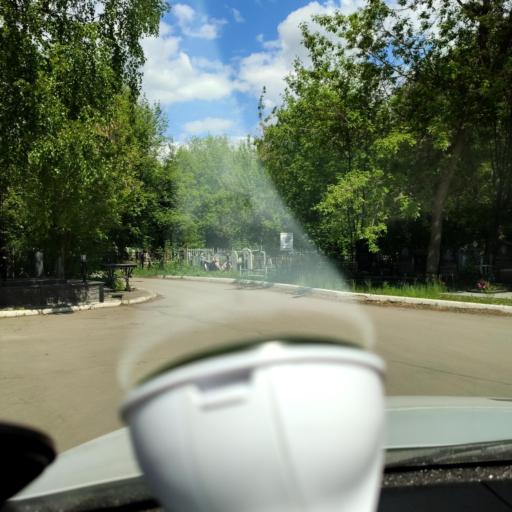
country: RU
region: Samara
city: Petra-Dubrava
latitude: 53.2746
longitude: 50.3210
